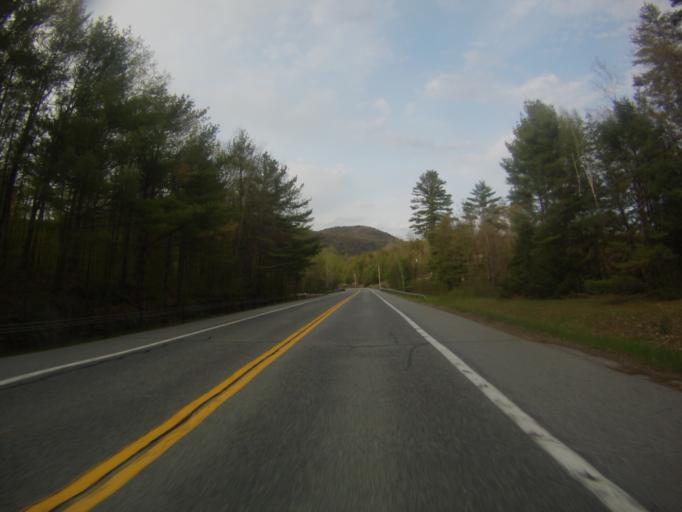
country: US
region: New York
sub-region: Warren County
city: Warrensburg
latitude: 43.7353
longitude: -73.6630
